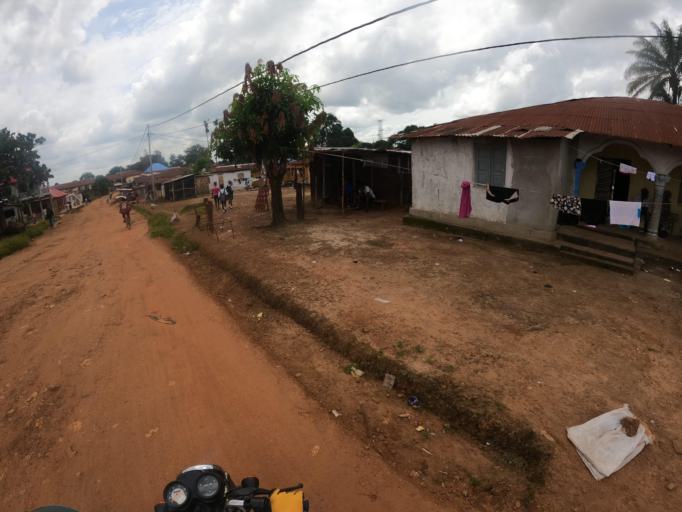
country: SL
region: Northern Province
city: Makeni
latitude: 8.9006
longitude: -12.0431
